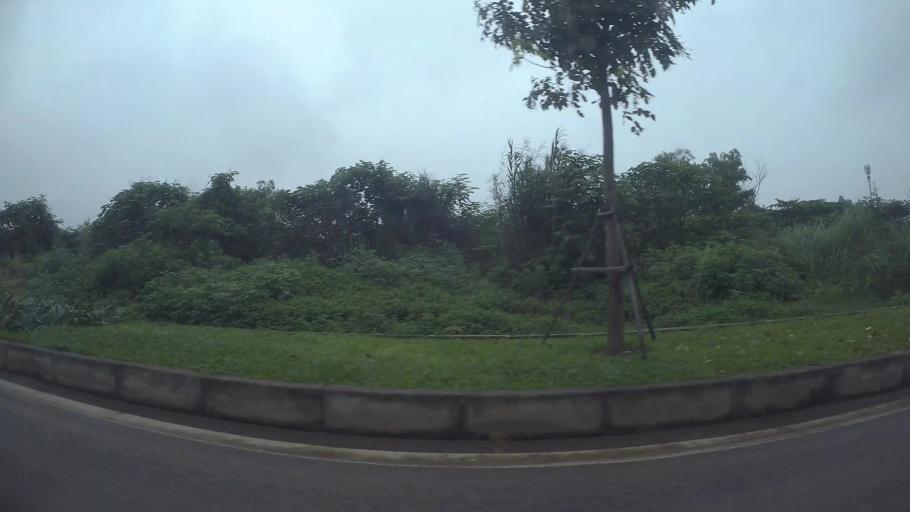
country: VN
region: Ha Noi
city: Van Dien
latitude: 20.9691
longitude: 105.8744
